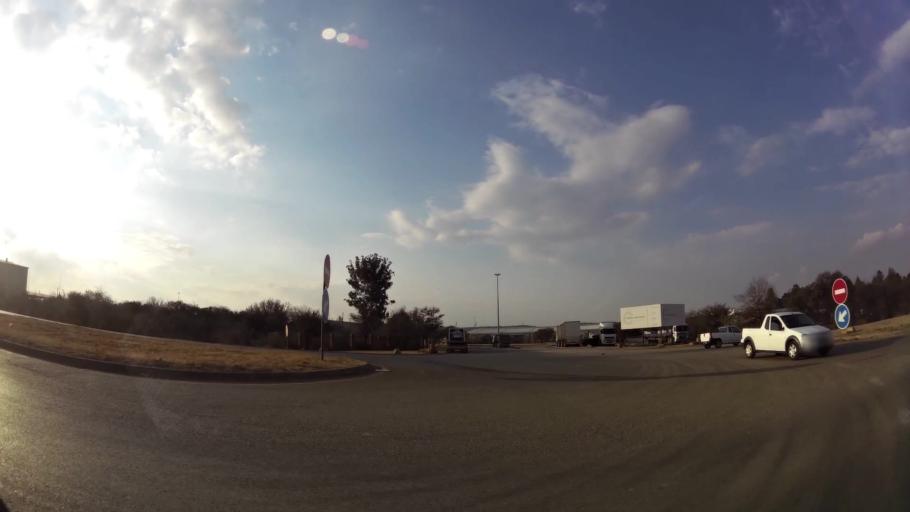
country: ZA
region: Gauteng
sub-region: Sedibeng District Municipality
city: Vereeniging
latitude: -26.6242
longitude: 27.8607
